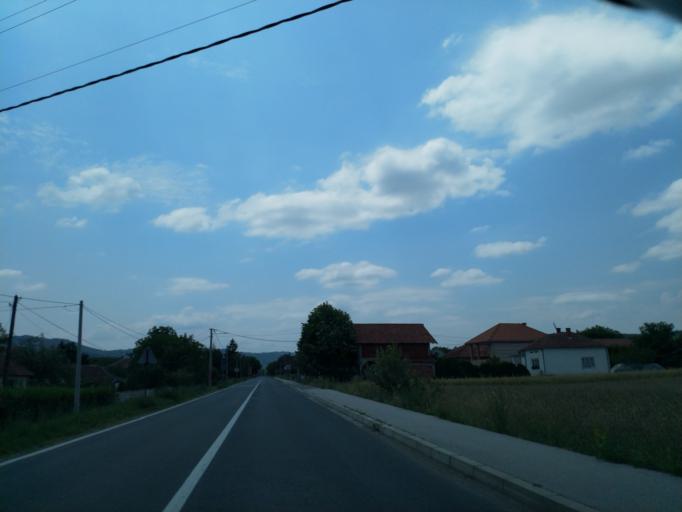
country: RS
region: Central Serbia
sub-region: Toplicki Okrug
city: Blace
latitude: 43.4463
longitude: 21.2305
